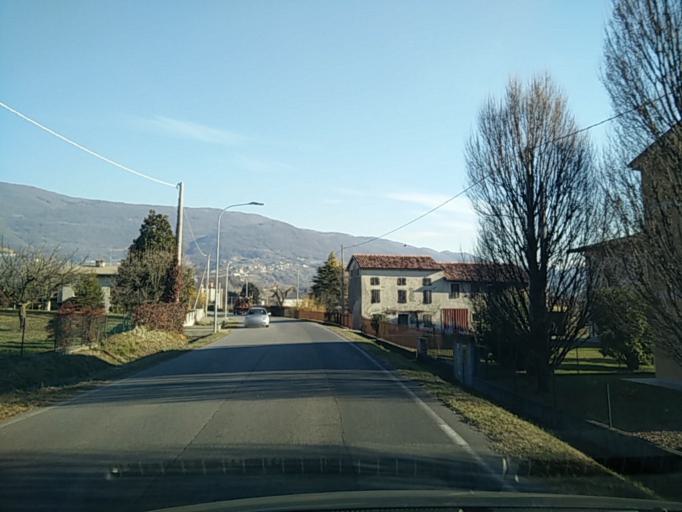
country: IT
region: Veneto
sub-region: Provincia di Treviso
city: Cappella Maggiore
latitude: 45.9725
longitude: 12.3702
